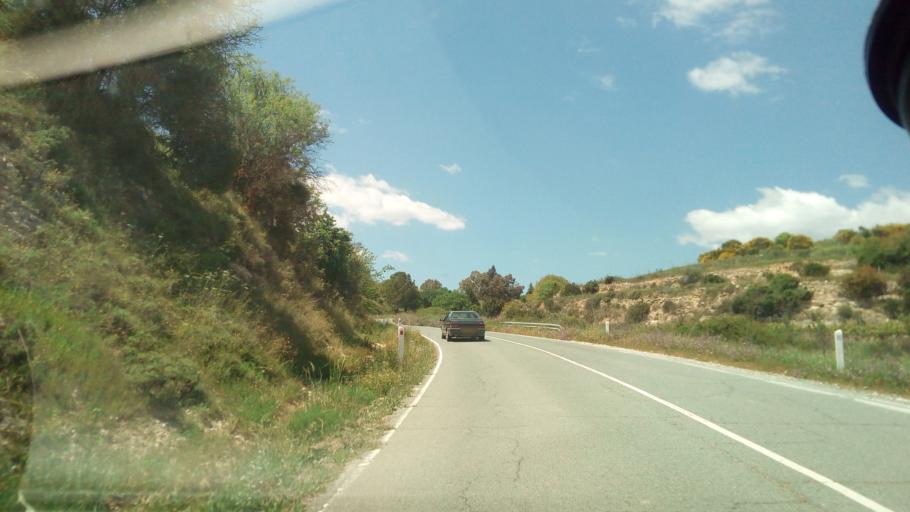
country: CY
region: Limassol
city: Pachna
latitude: 34.8137
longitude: 32.7883
